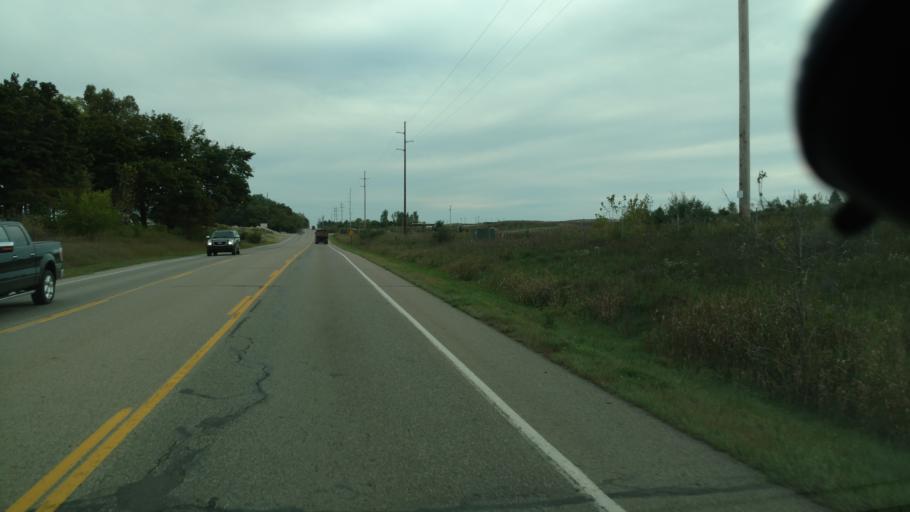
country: US
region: Michigan
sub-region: Ingham County
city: Lansing
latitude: 42.7799
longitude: -84.5231
